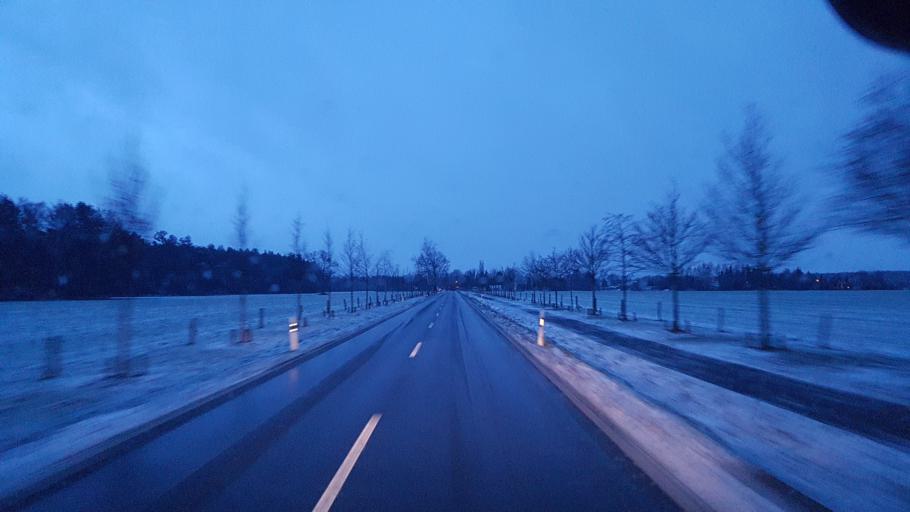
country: DE
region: Brandenburg
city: Briesen
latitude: 51.8247
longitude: 14.2529
